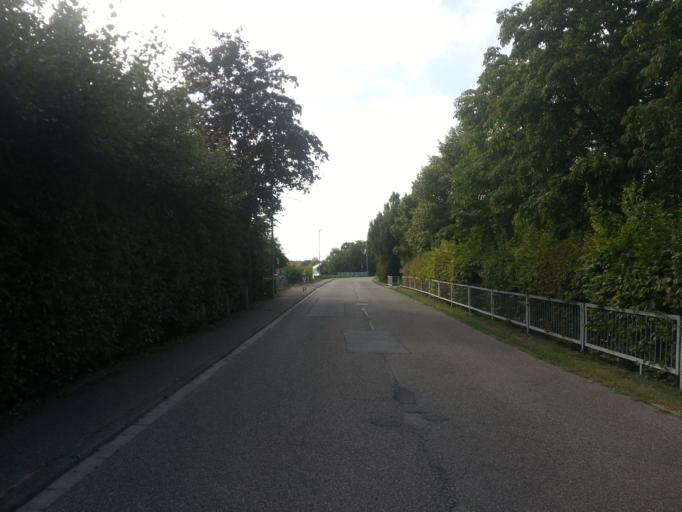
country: DE
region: Baden-Wuerttemberg
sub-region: Karlsruhe Region
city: Ilvesheim
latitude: 49.4788
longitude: 8.5678
